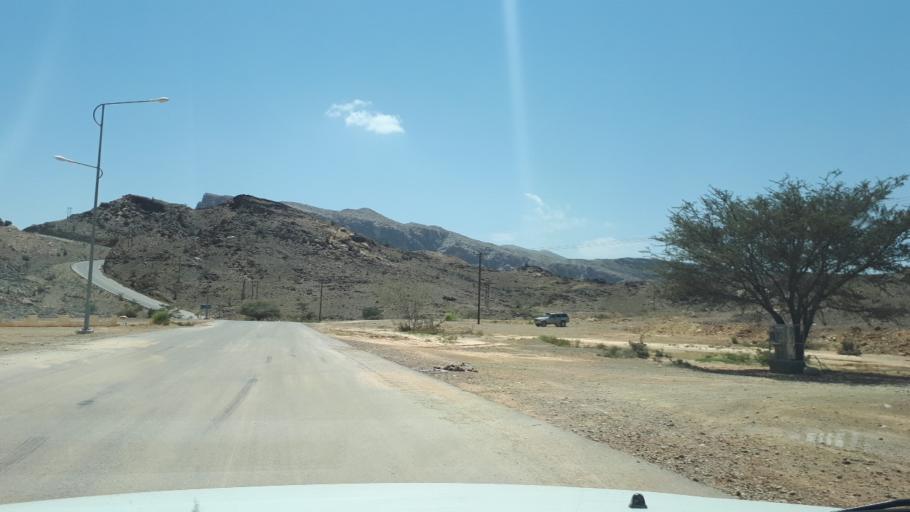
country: OM
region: Muhafazat ad Dakhiliyah
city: Bahla'
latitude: 23.2377
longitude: 57.1494
